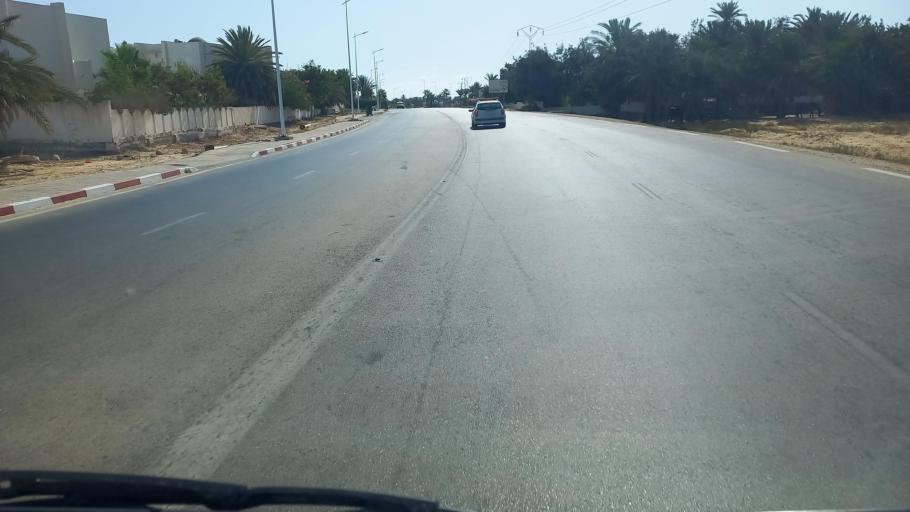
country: TN
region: Madanin
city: Midoun
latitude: 33.8370
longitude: 10.9970
